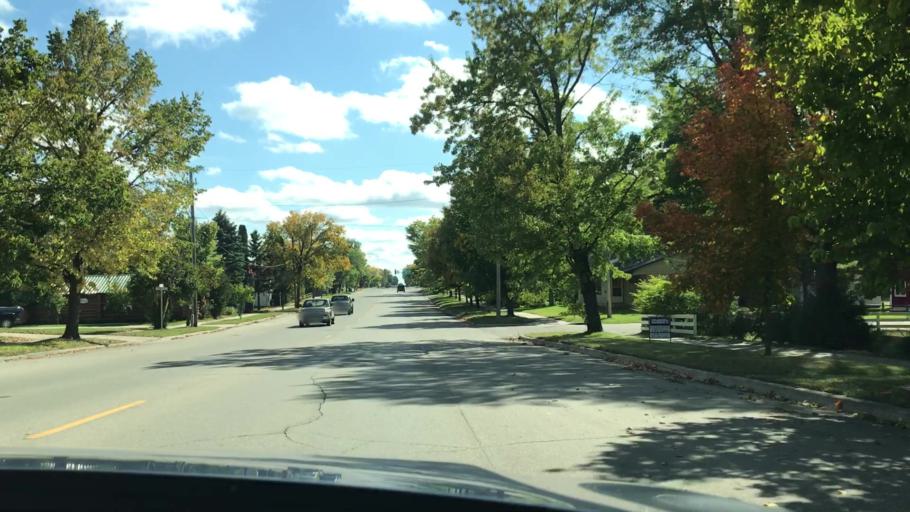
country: US
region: Minnesota
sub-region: Hubbard County
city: Park Rapids
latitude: 46.9249
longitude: -95.0586
